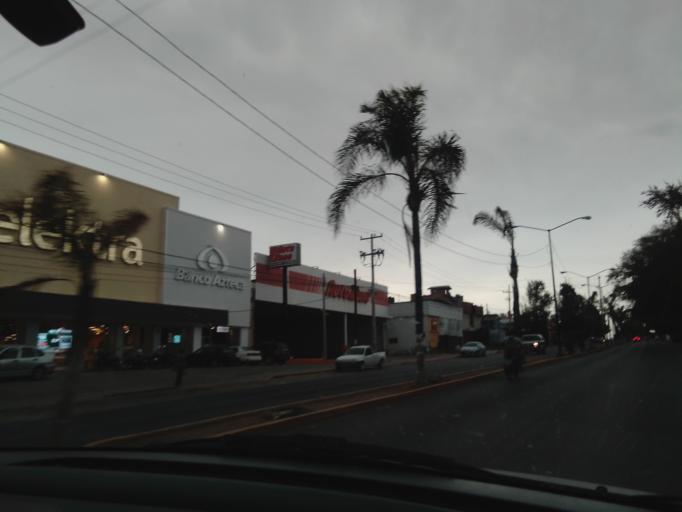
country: MX
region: Guanajuato
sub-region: Dolores Hidalgo Cuna de la Independencia Nacional
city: Dolores Hidalgo Cuna de la Independencia Nacional
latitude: 21.1565
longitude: -100.9210
